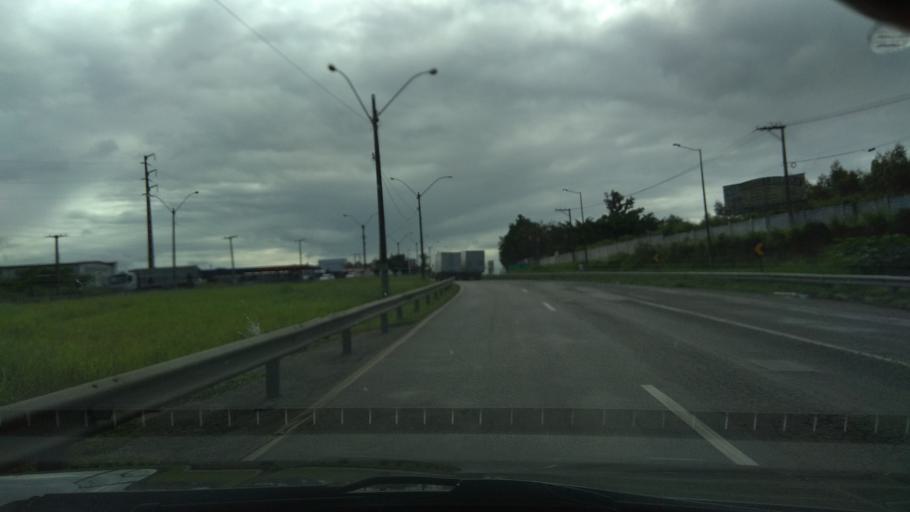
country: BR
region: Bahia
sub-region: Feira De Santana
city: Feira de Santana
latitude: -12.2988
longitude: -38.9002
